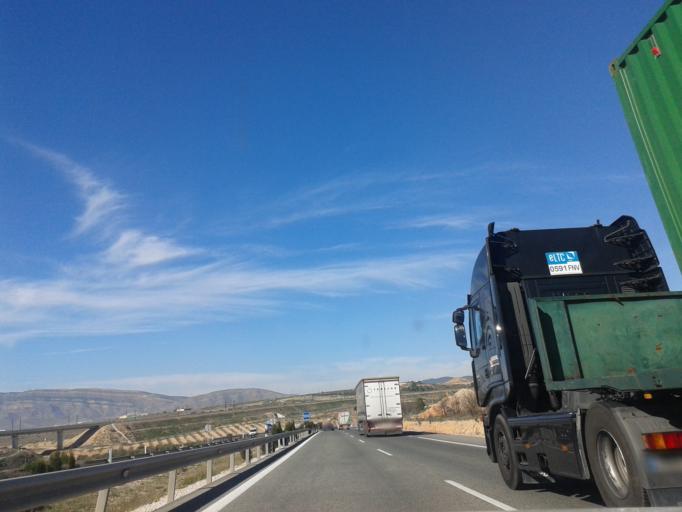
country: ES
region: Castille-La Mancha
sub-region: Provincia de Albacete
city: Caudete
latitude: 38.7044
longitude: -0.9248
